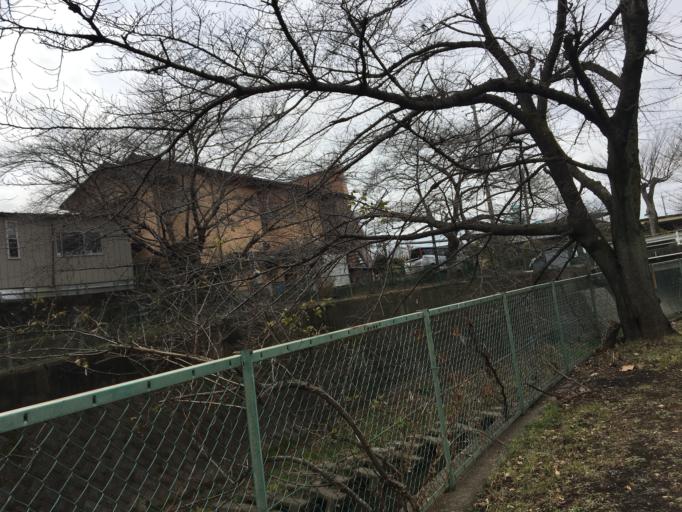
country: JP
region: Saitama
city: Oi
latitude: 35.8047
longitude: 139.5232
